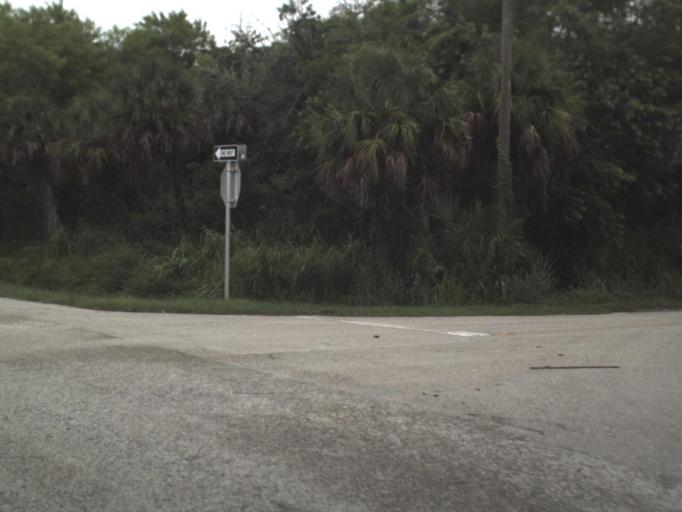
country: US
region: Florida
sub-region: Manatee County
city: Memphis
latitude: 27.6160
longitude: -82.5396
